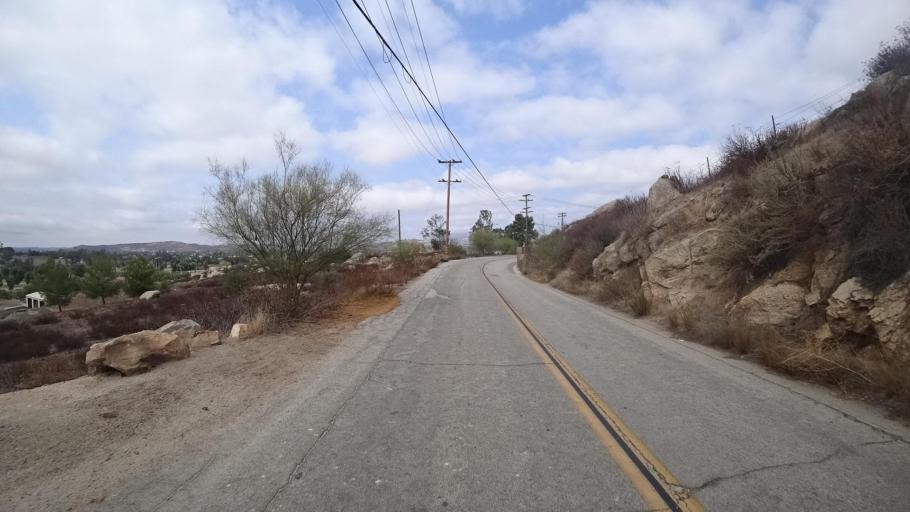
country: US
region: California
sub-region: San Diego County
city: Ramona
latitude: 33.0505
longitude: -116.8565
